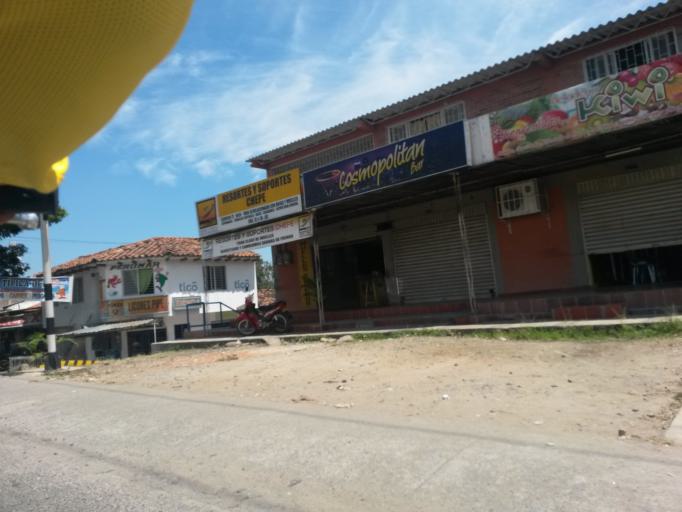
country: CO
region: Cauca
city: Santander de Quilichao
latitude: 3.0124
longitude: -76.4840
